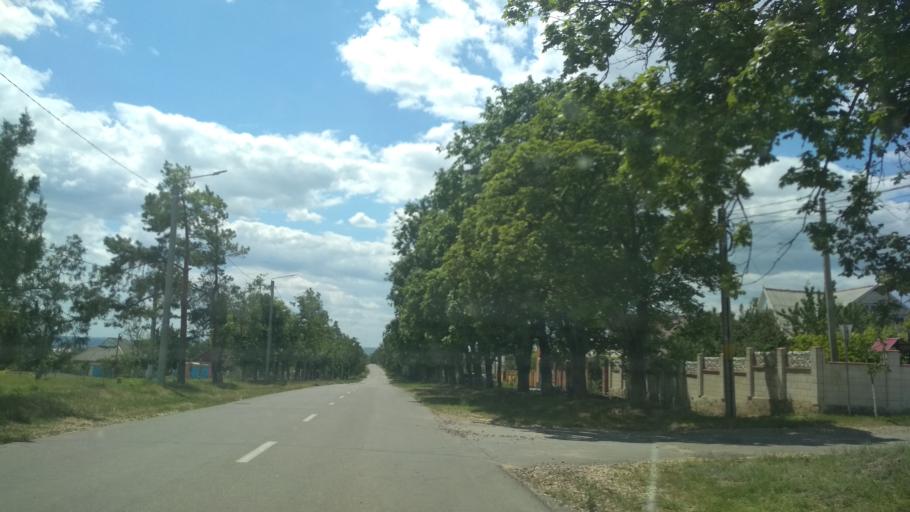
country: MD
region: Criuleni
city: Criuleni
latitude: 47.1762
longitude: 29.1995
